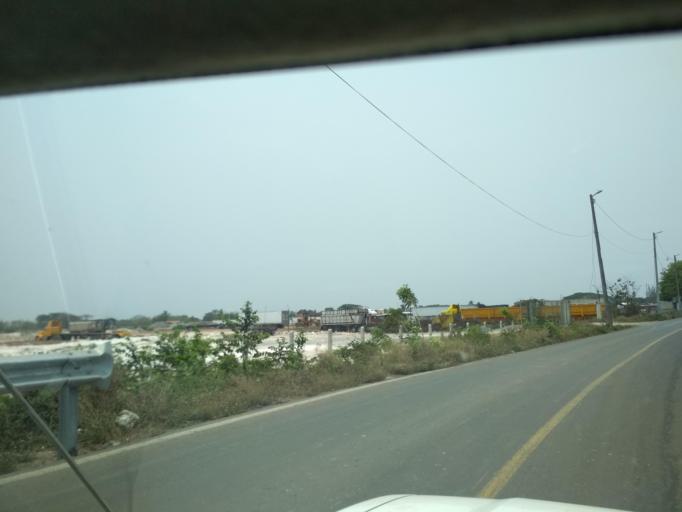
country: MX
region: Veracruz
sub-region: Veracruz
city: Delfino Victoria (Santa Fe)
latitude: 19.2078
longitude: -96.2640
